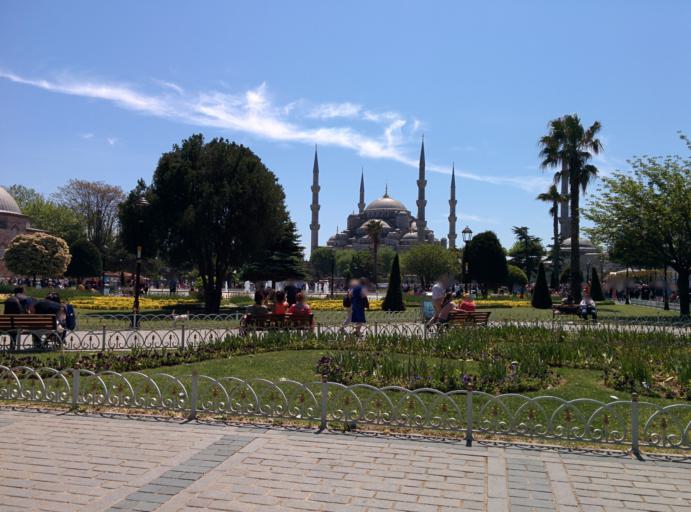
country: TR
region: Istanbul
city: Eminoenue
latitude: 41.0100
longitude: 28.9791
